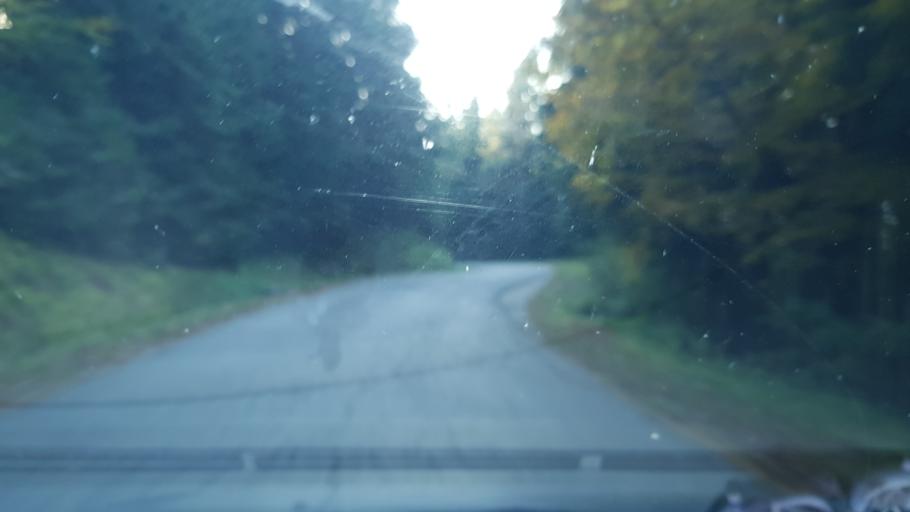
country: SI
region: Slovenj Gradec
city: Legen
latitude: 46.4859
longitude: 15.1604
